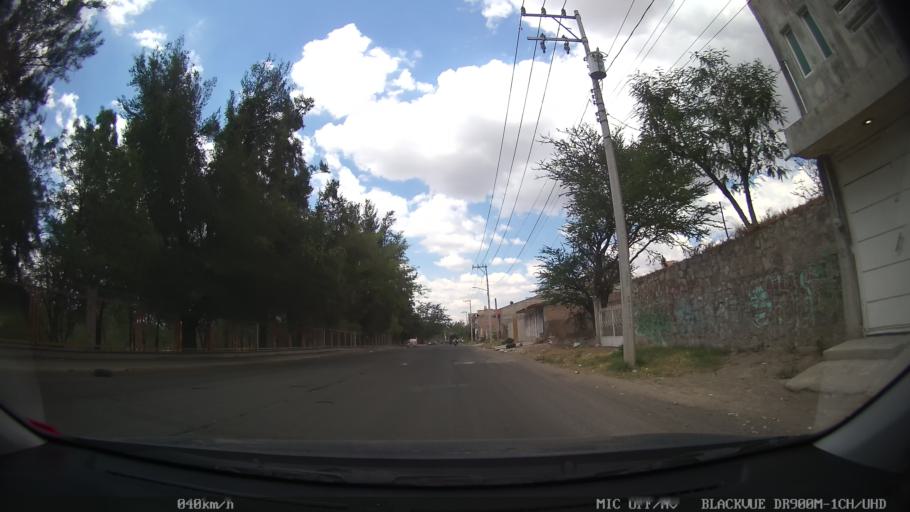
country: MX
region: Jalisco
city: Tlaquepaque
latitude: 20.6638
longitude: -103.2679
